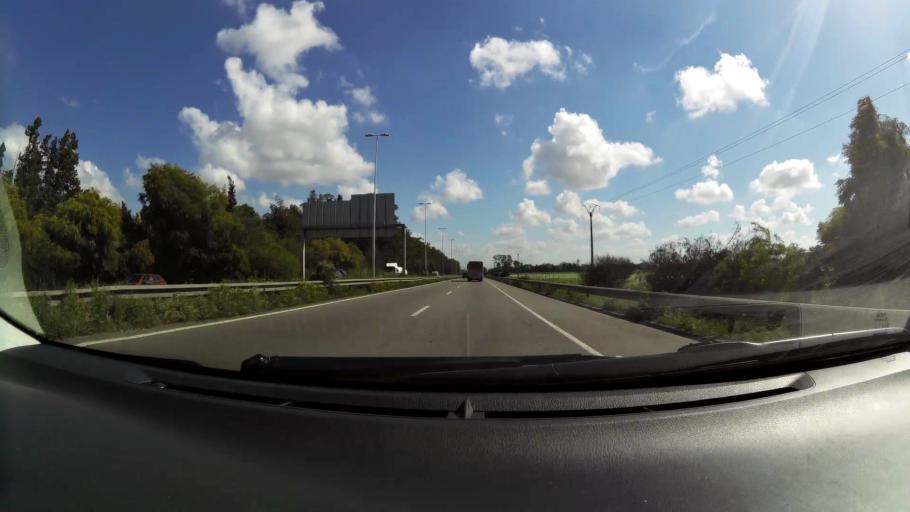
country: MA
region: Grand Casablanca
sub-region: Nouaceur
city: Bouskoura
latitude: 33.4770
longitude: -7.6334
